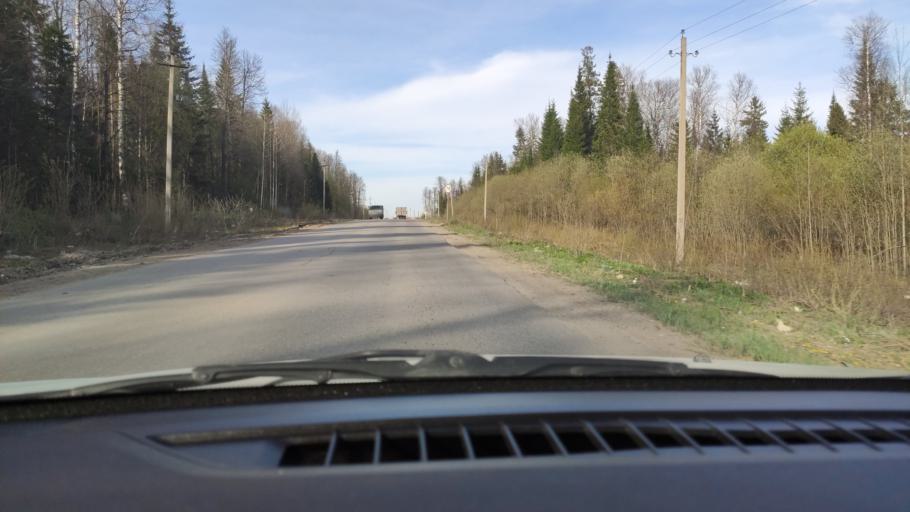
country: RU
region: Perm
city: Novyye Lyady
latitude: 57.9529
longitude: 56.5120
